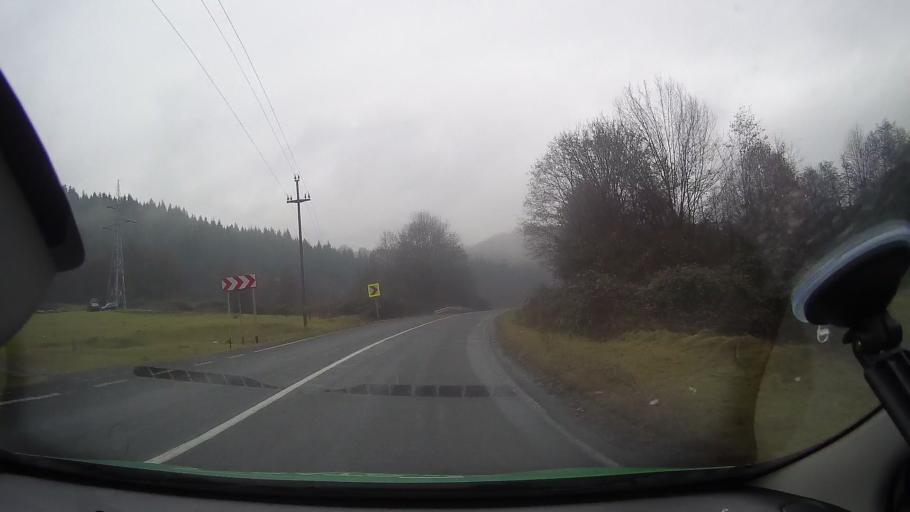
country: RO
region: Arad
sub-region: Comuna Plescuta
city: Plescuta
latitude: 46.3152
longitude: 22.4565
